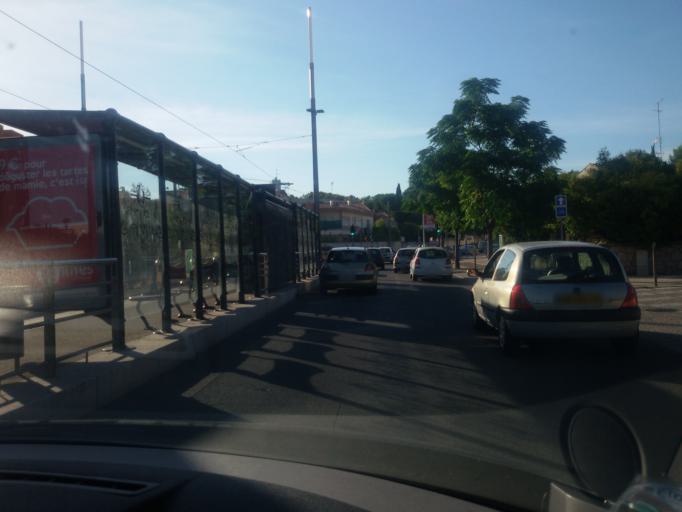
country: FR
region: Languedoc-Roussillon
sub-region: Departement de l'Herault
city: Montpellier
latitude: 43.5921
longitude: 3.8806
